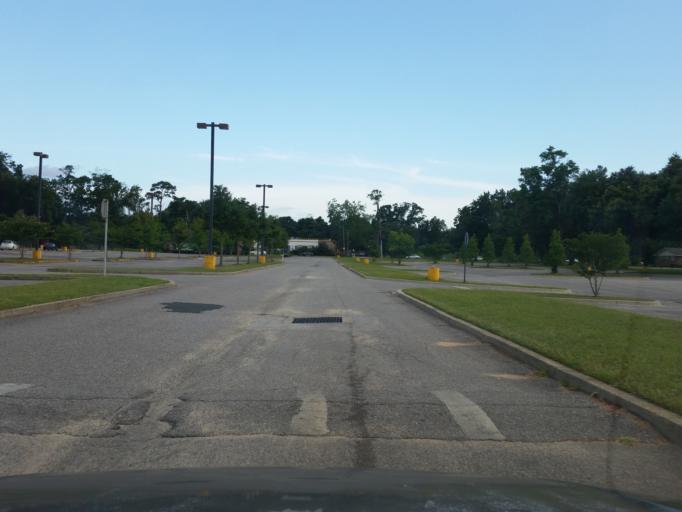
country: US
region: Florida
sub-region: Escambia County
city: Ferry Pass
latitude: 30.5127
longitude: -87.2240
